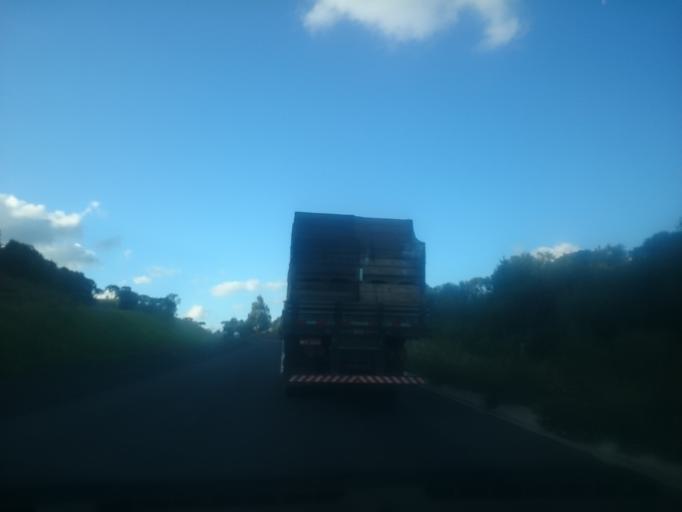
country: BR
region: Santa Catarina
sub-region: Sao Joaquim
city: Sao Joaquim
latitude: -28.0652
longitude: -50.0733
